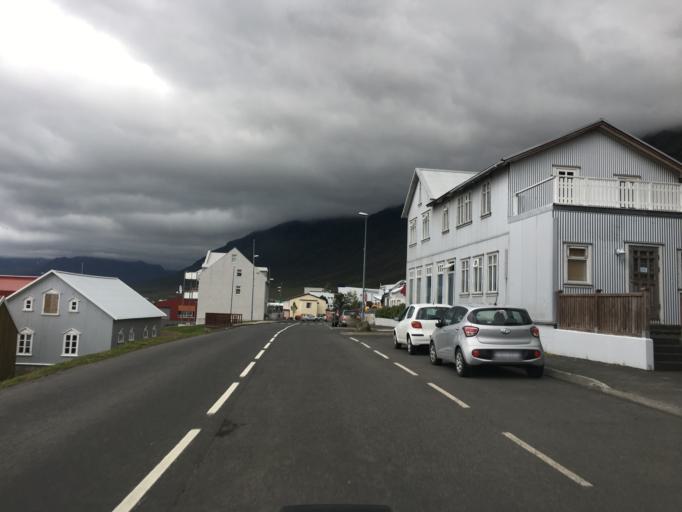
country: IS
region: East
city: Neskaupstadur
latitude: 65.1475
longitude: -13.6844
